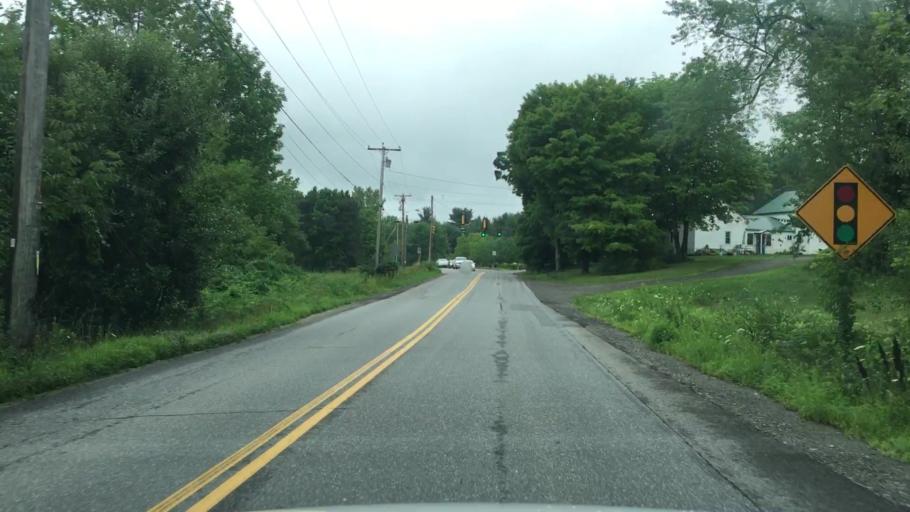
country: US
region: Maine
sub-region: Kennebec County
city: Augusta
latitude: 44.3190
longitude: -69.7358
